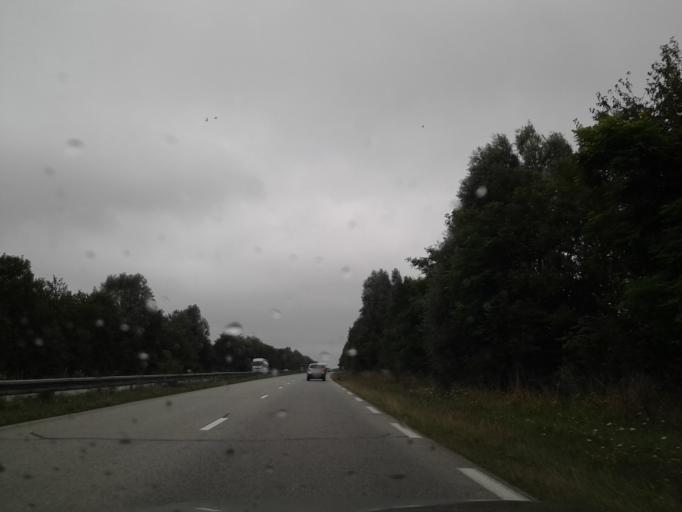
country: FR
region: Lower Normandy
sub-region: Departement de la Manche
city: Montebourg
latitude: 49.4795
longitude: -1.3819
